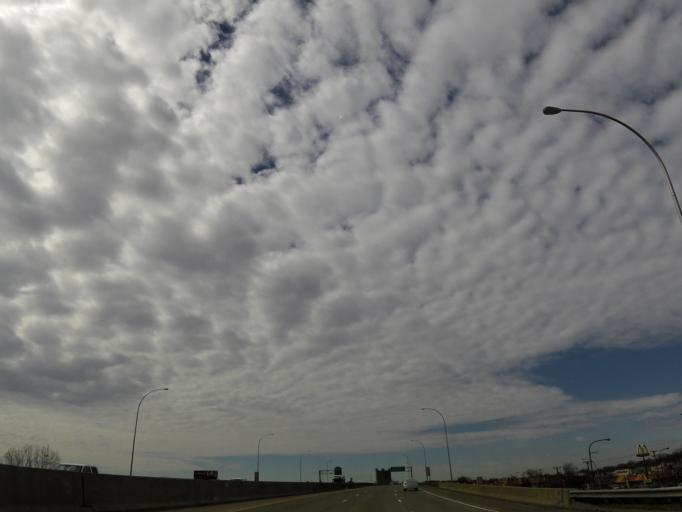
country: US
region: Minnesota
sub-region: Ramsey County
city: Lauderdale
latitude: 45.0011
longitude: -93.2262
